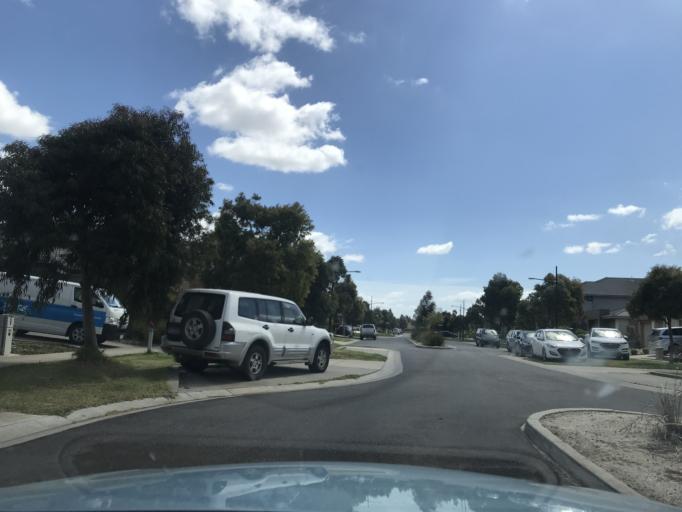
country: AU
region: Victoria
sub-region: Wyndham
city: Williams Landing
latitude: -37.8623
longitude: 144.7440
